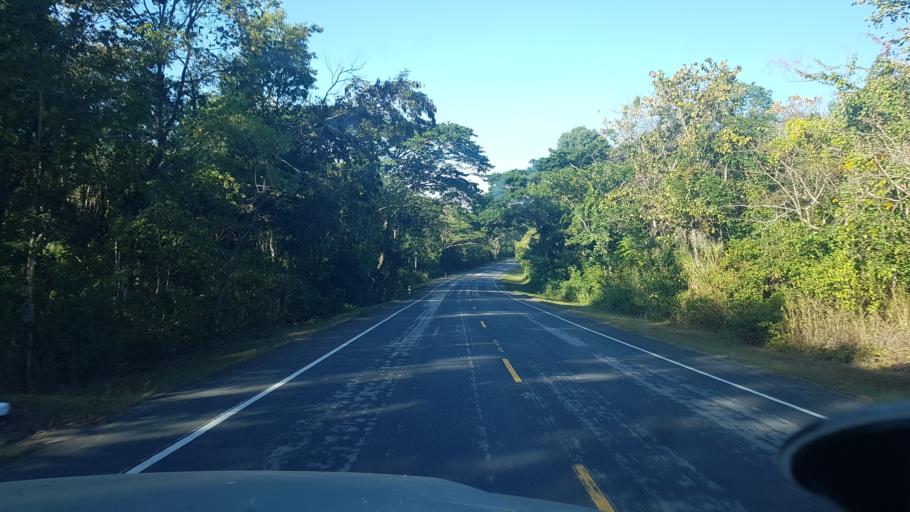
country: TH
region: Phetchabun
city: Lom Sak
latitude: 16.7364
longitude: 101.4370
